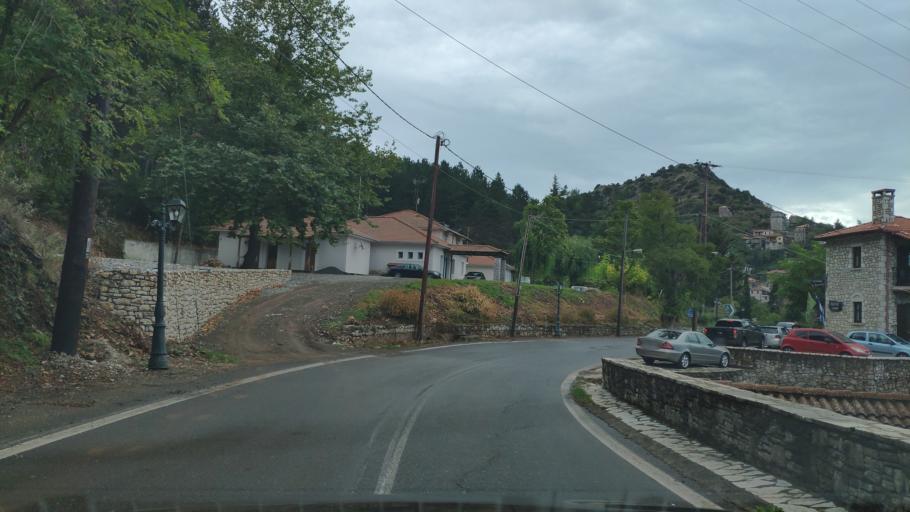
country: GR
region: Peloponnese
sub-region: Nomos Arkadias
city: Dimitsana
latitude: 37.5991
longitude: 22.0407
